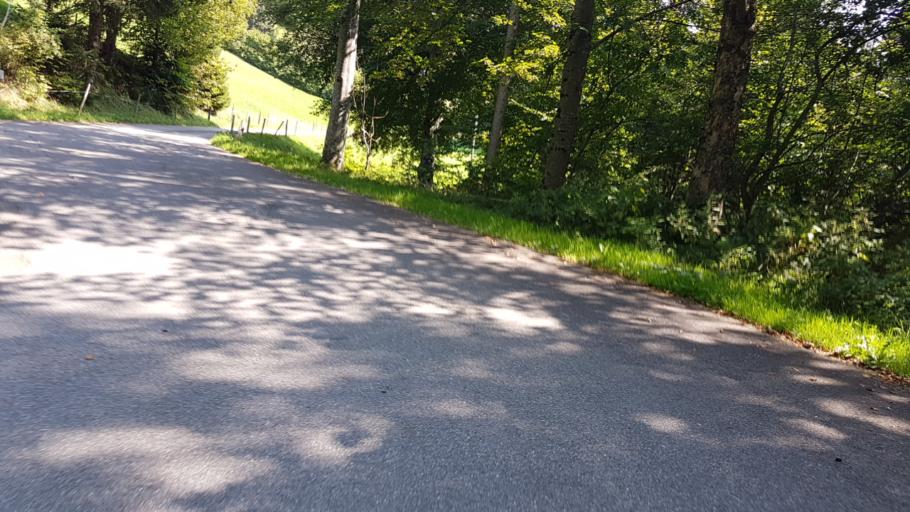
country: CH
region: Bern
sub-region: Frutigen-Niedersimmental District
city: Aeschi
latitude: 46.5971
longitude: 7.7167
